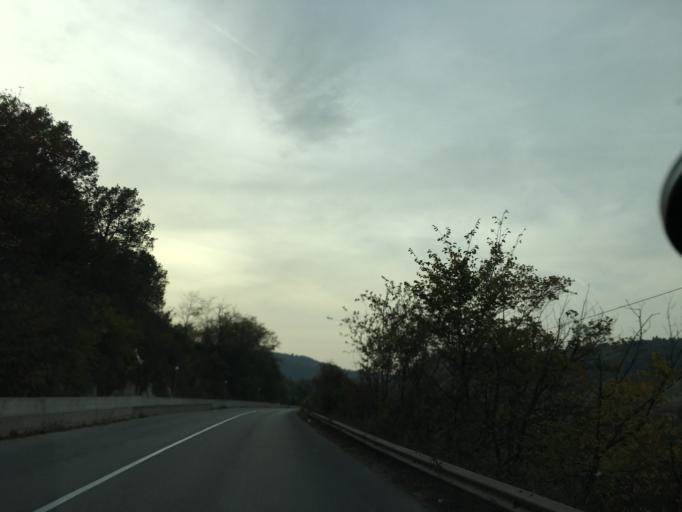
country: BG
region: Pazardzhik
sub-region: Obshtina Belovo
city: Belovo
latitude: 42.2288
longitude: 23.9705
